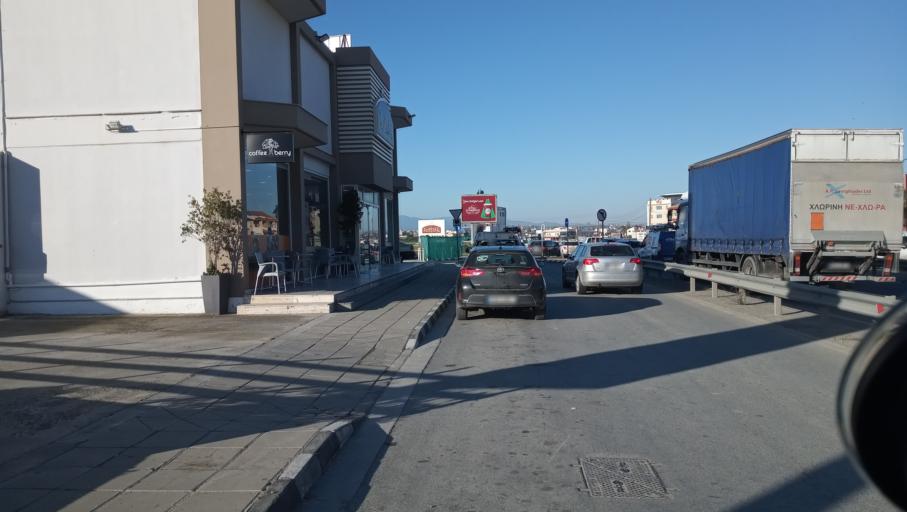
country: CY
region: Lefkosia
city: Tseri
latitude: 35.1218
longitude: 33.3402
